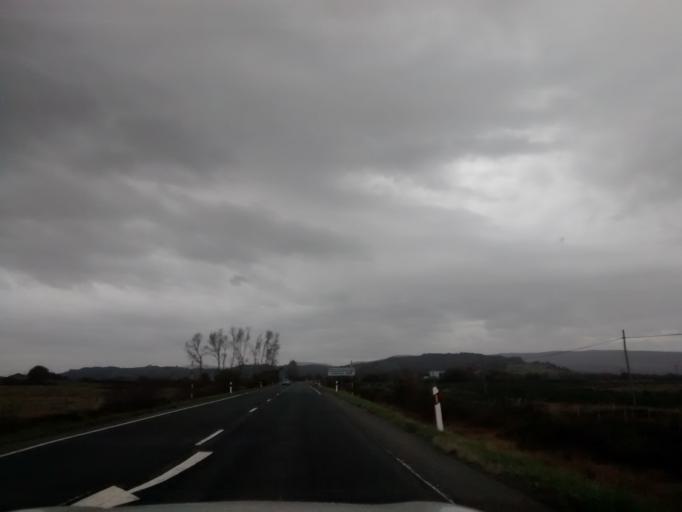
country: ES
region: Castille and Leon
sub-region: Provincia de Burgos
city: Arija
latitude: 43.0189
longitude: -3.8553
